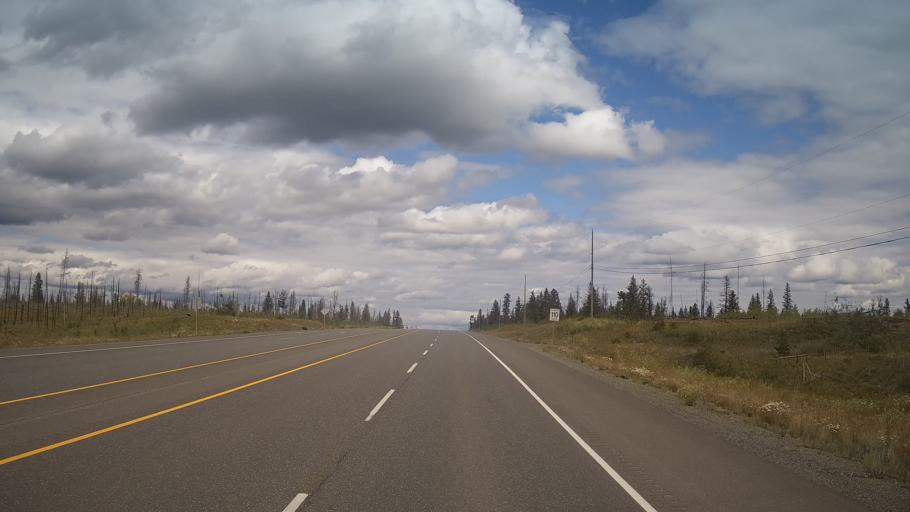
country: CA
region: British Columbia
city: Cache Creek
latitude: 51.3253
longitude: -121.3863
